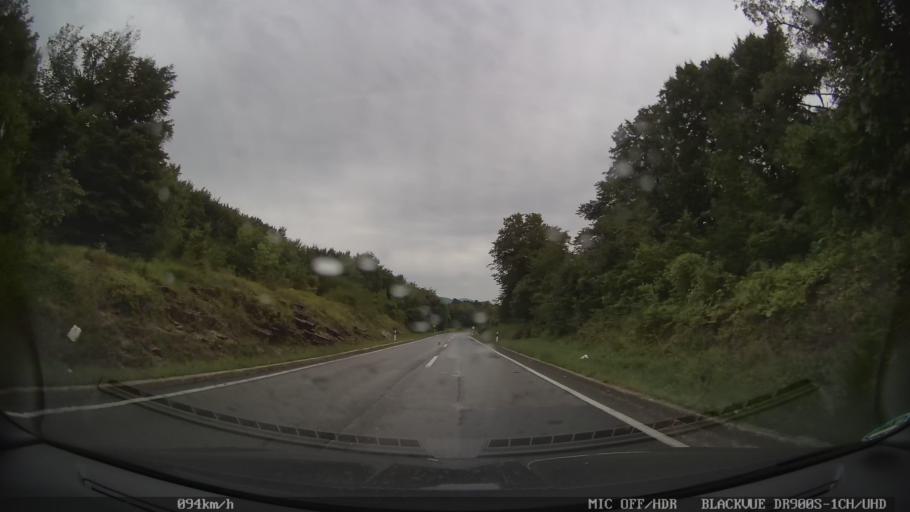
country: HR
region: Licko-Senjska
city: Brinje
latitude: 44.9623
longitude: 15.0859
